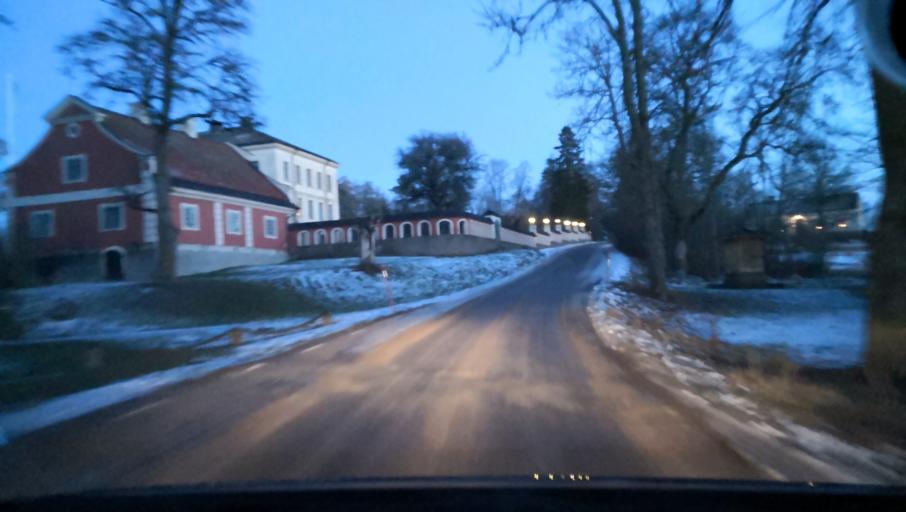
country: SE
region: Soedermanland
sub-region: Katrineholms Kommun
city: Katrineholm
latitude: 59.0847
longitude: 16.3164
